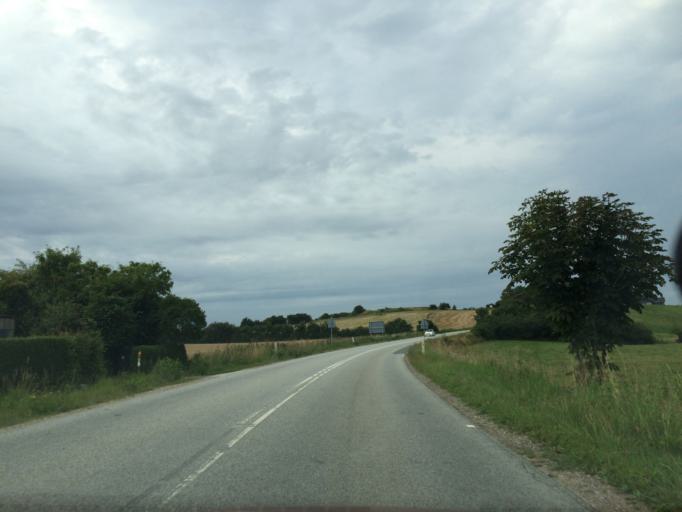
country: DK
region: South Denmark
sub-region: Sonderborg Kommune
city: Broager
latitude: 54.8948
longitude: 9.6736
